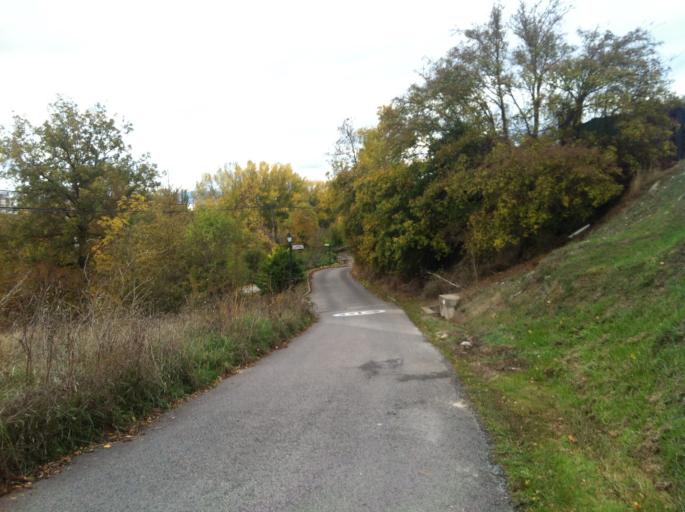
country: ES
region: Basque Country
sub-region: Provincia de Alava
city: Gasteiz / Vitoria
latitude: 42.8306
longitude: -2.7000
